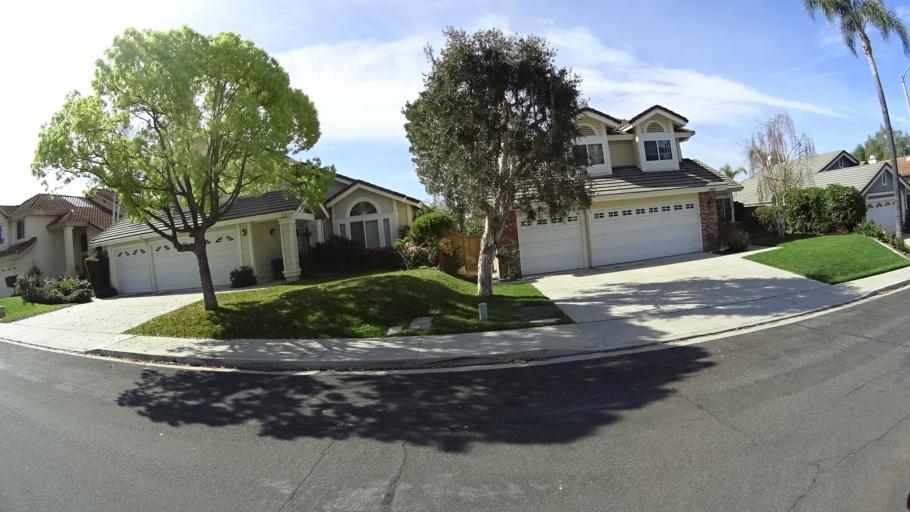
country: US
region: California
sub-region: Ventura County
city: Thousand Oaks
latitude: 34.2136
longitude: -118.8382
